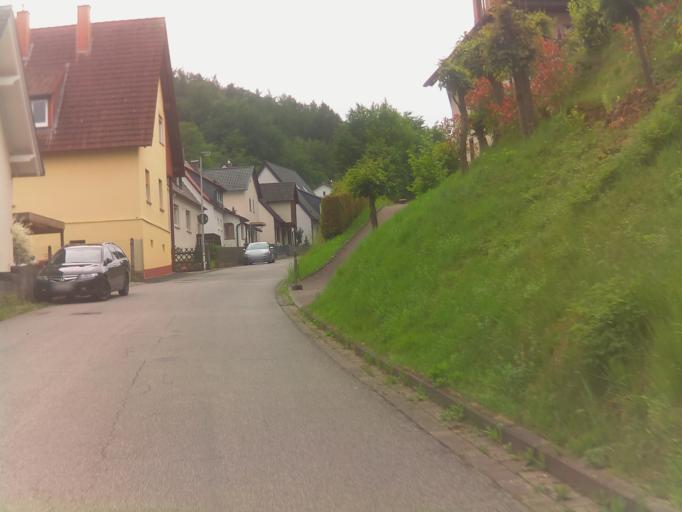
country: DE
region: Bavaria
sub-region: Regierungsbezirk Unterfranken
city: Mombris
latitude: 50.0858
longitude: 9.1393
